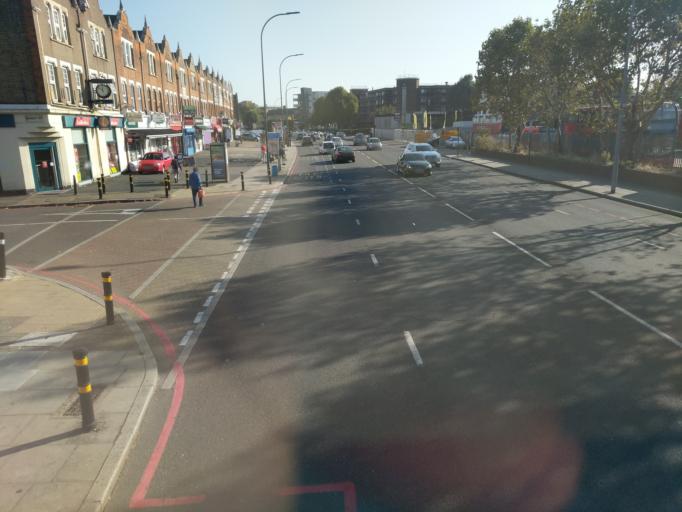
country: GB
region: England
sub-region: Greater London
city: Catford
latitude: 51.4344
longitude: -0.0178
